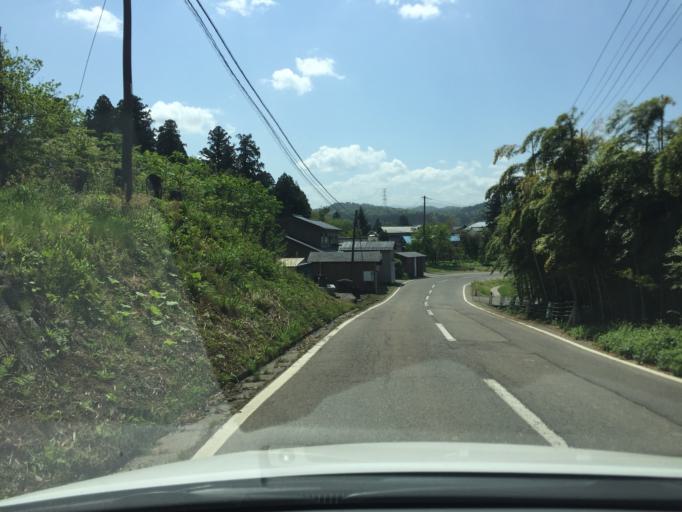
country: JP
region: Niigata
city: Tochio-honcho
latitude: 37.5496
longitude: 139.0866
